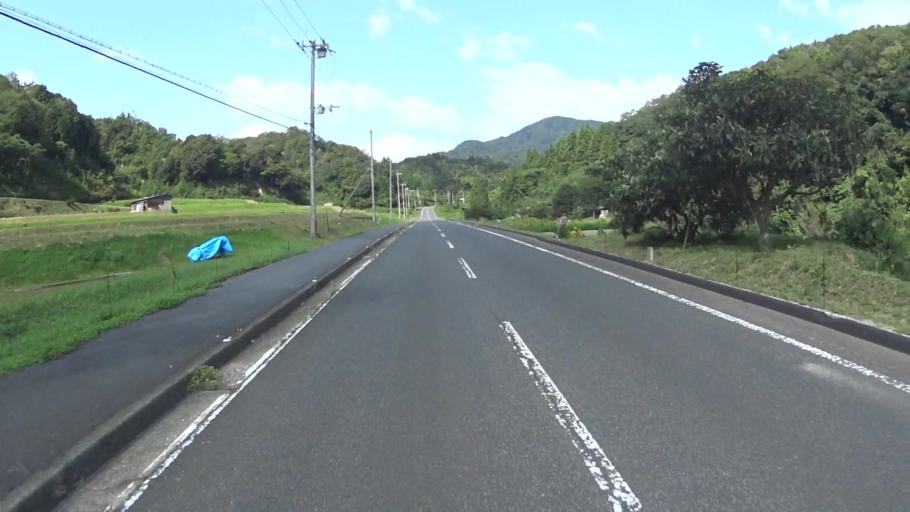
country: JP
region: Kyoto
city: Miyazu
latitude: 35.6268
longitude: 135.2380
